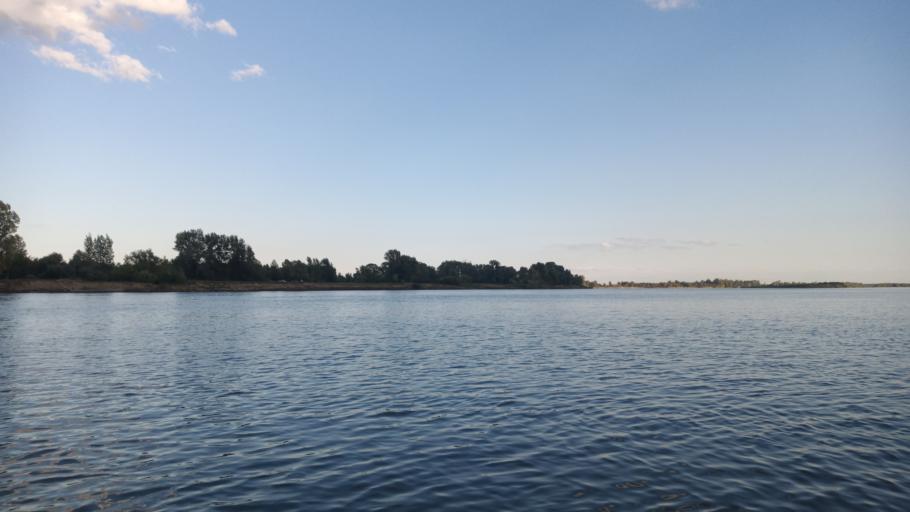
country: RU
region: Altai Krai
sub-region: Gorod Barnaulskiy
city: Barnaul
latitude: 53.3667
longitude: 83.8115
